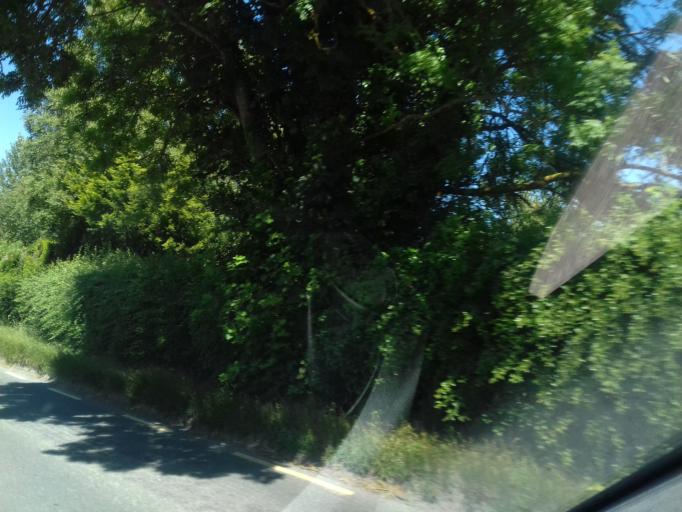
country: IE
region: Leinster
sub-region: Fingal County
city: Swords
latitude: 53.4789
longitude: -6.2760
